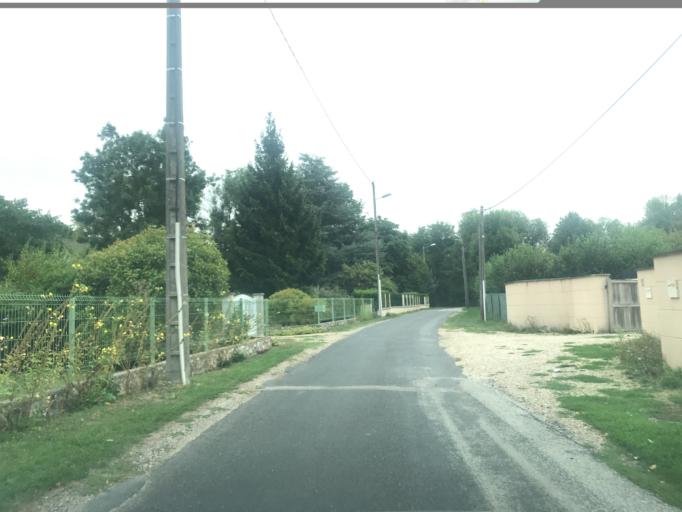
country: FR
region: Haute-Normandie
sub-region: Departement de l'Eure
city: Houlbec-Cocherel
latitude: 49.0719
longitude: 1.2901
